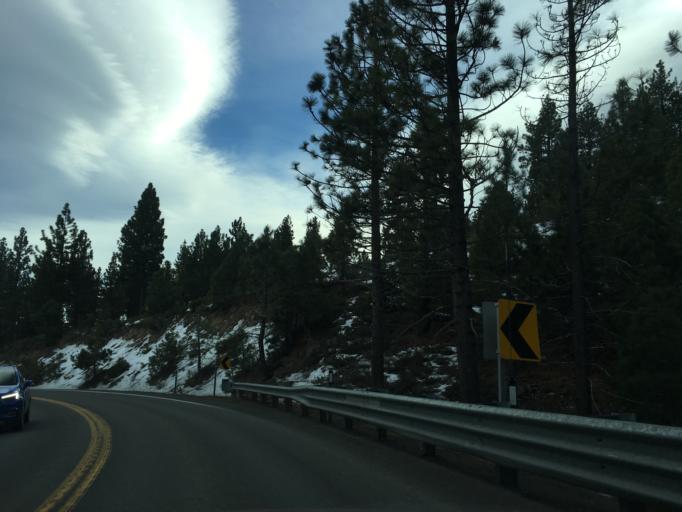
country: US
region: Nevada
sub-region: Washoe County
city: Incline Village
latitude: 39.3407
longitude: -119.8629
